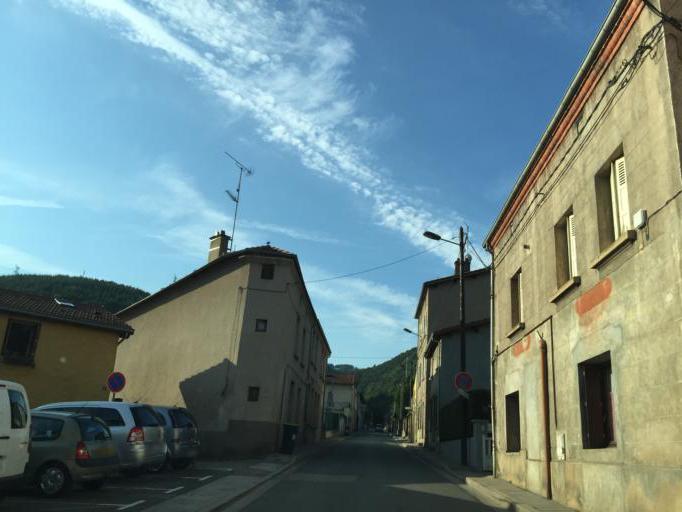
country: FR
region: Rhone-Alpes
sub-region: Departement de la Loire
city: Saint-Jean-Bonnefonds
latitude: 45.4281
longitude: 4.4351
